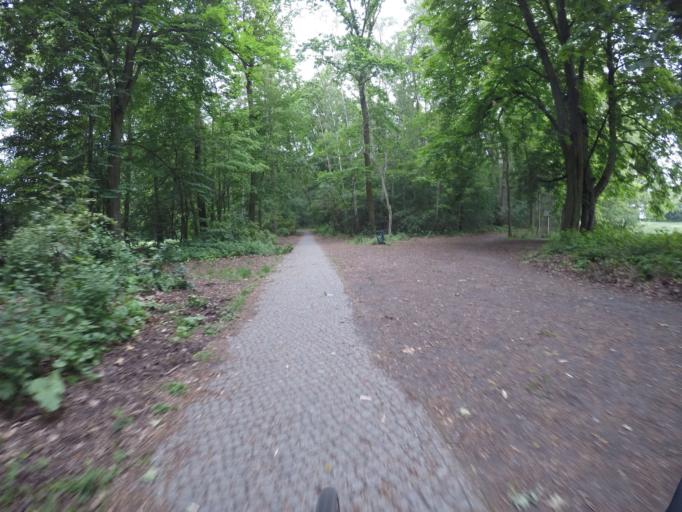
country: DE
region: Berlin
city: Wittenau
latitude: 52.5981
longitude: 13.3146
